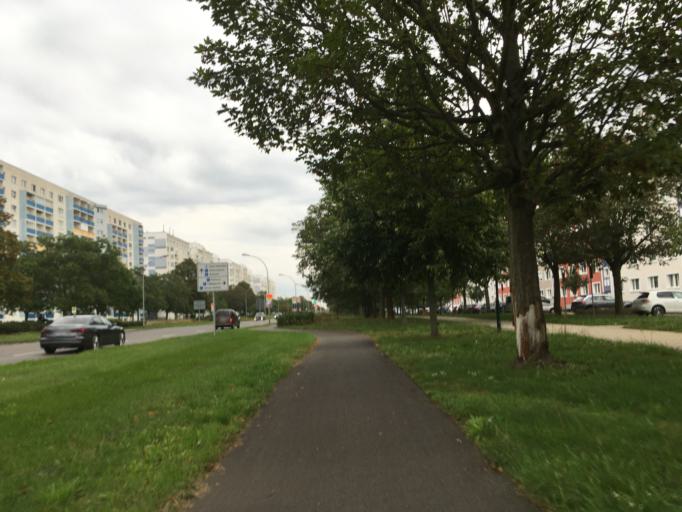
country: DE
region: Brandenburg
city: Schwedt (Oder)
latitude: 53.0640
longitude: 14.2811
